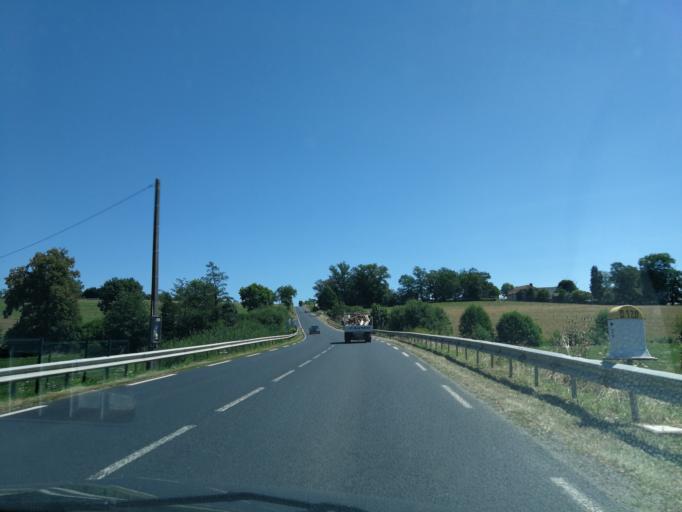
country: FR
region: Auvergne
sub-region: Departement du Cantal
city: Naucelles
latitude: 44.9352
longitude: 2.3948
